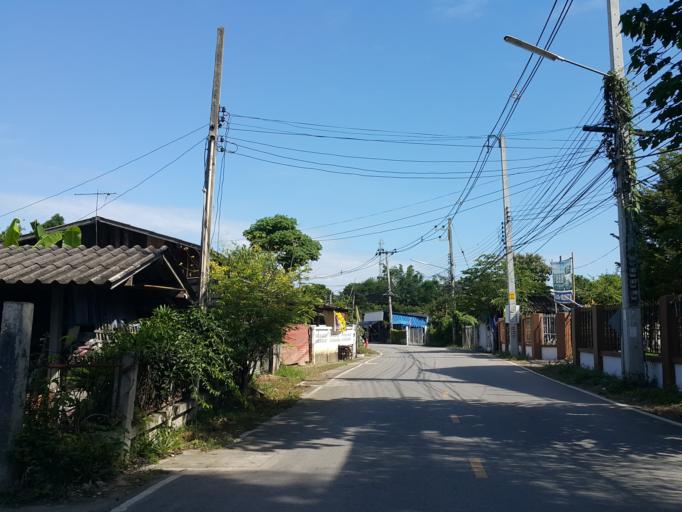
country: TH
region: Chiang Mai
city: San Sai
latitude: 18.8056
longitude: 99.0453
